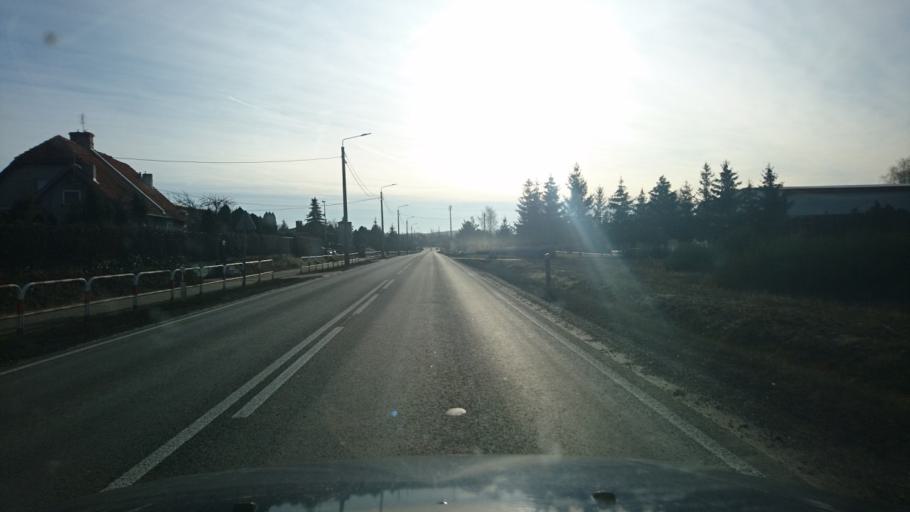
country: PL
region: Greater Poland Voivodeship
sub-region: Powiat ostrzeszowski
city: Ostrzeszow
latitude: 51.4403
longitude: 17.9142
